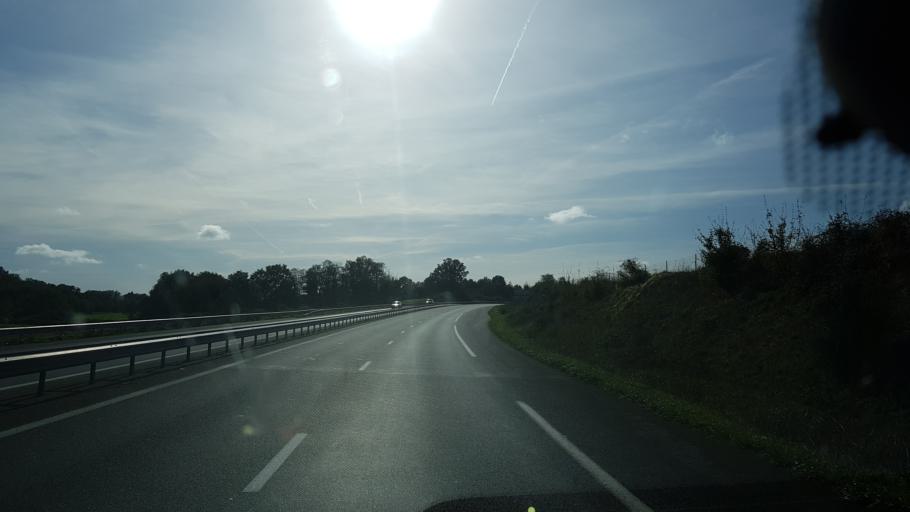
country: FR
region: Poitou-Charentes
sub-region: Departement de la Charente
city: Rivieres
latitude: 45.7459
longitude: 0.3653
